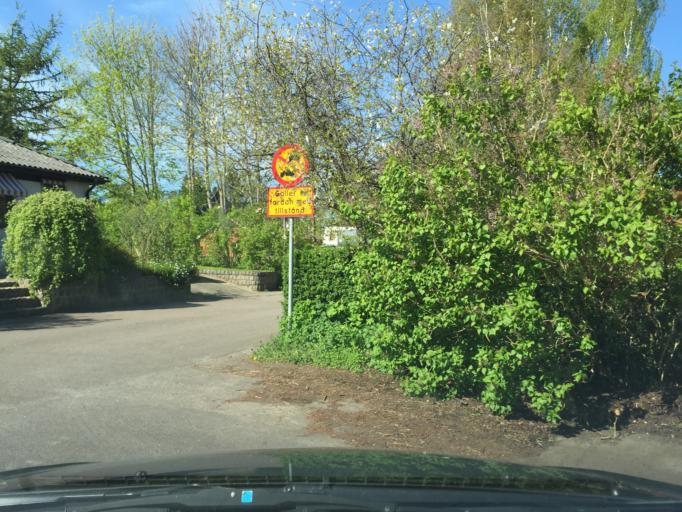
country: SE
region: Skane
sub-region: Sjobo Kommun
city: Blentarp
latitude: 55.5813
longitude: 13.6054
